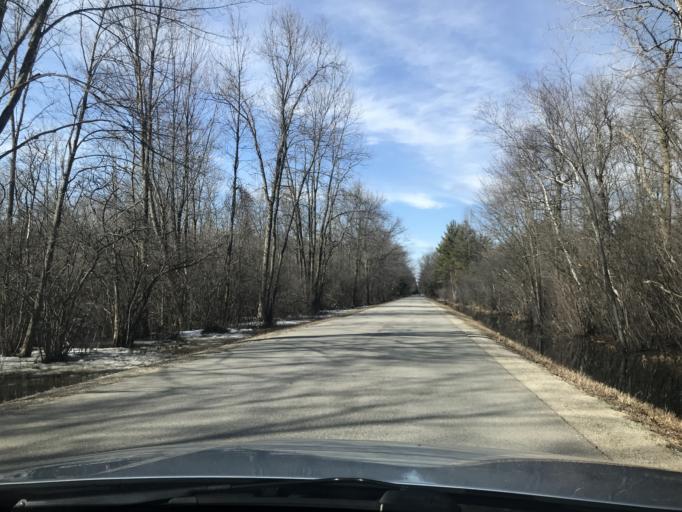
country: US
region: Wisconsin
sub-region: Marinette County
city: Marinette
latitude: 45.0213
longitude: -87.6672
